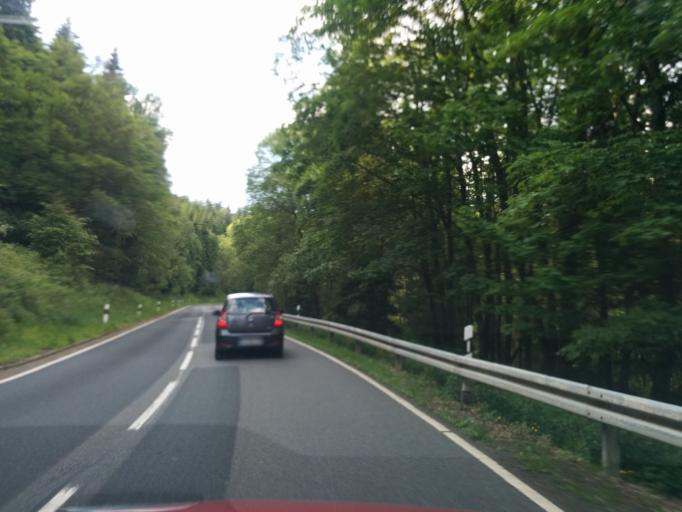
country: DE
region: Lower Saxony
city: Wieda
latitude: 51.6707
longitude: 10.5936
